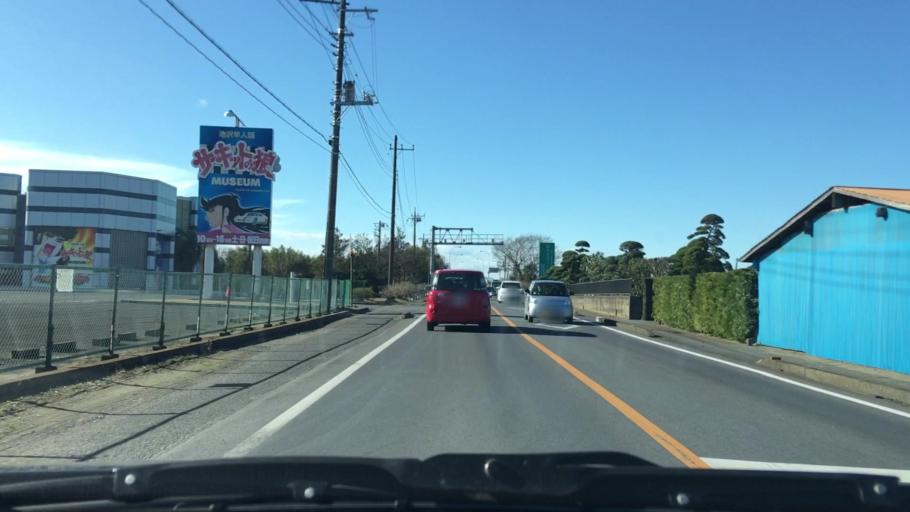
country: JP
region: Chiba
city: Omigawa
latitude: 35.8754
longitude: 140.6270
